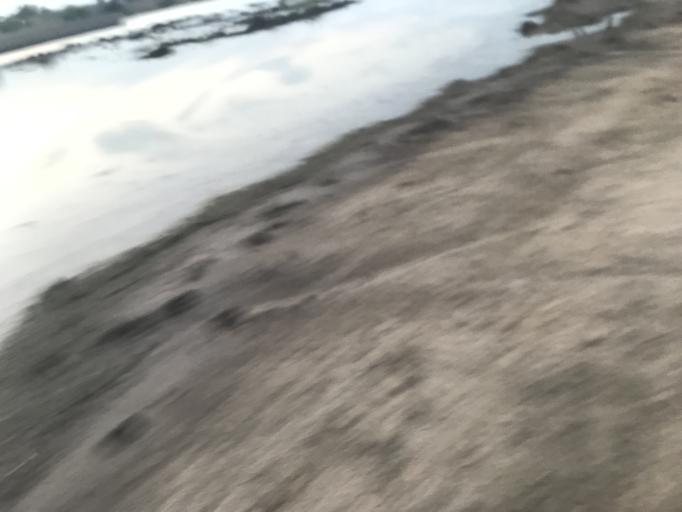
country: SN
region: Saint-Louis
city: Saint-Louis
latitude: 16.0550
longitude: -16.4087
